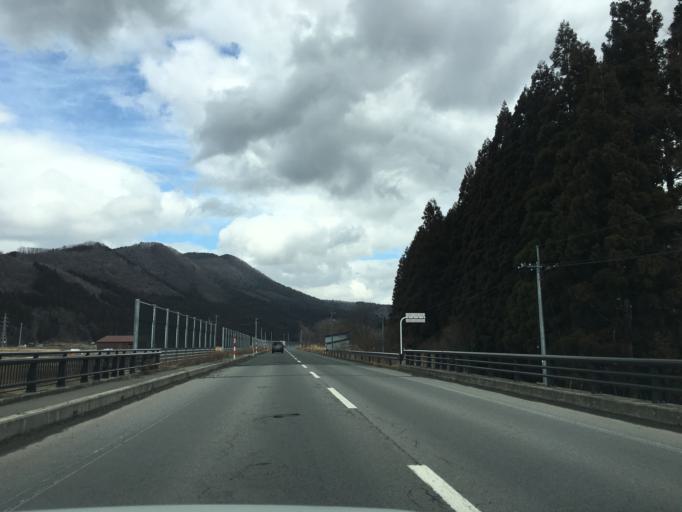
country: JP
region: Akita
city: Hanawa
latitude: 40.2260
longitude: 140.6786
